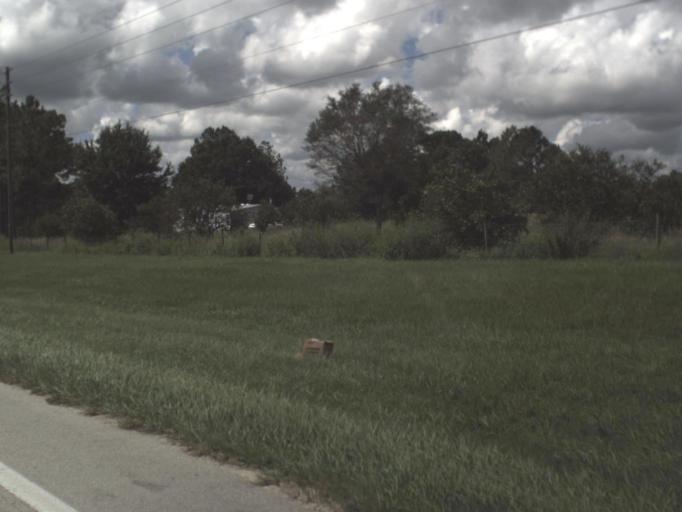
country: US
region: Florida
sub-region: Polk County
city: Polk City
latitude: 28.3122
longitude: -81.8353
